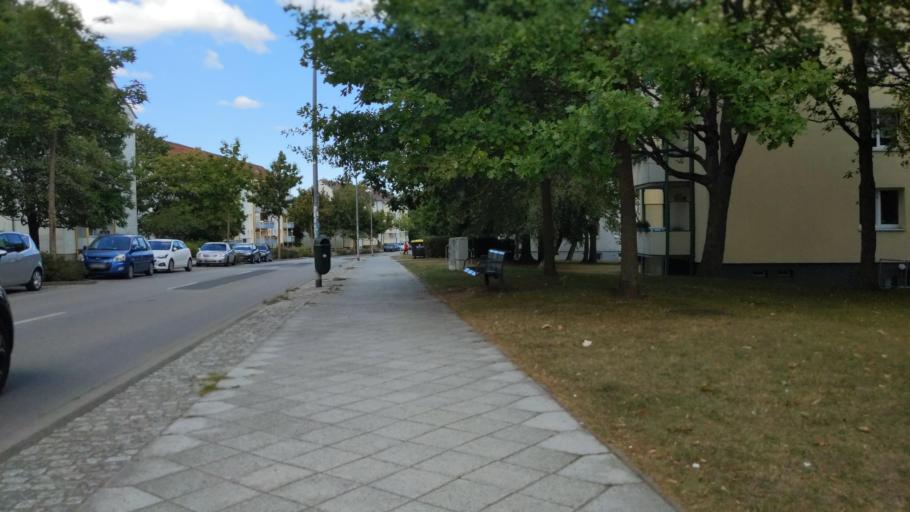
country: DE
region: Mecklenburg-Vorpommern
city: Wismar
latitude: 53.9080
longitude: 11.4279
